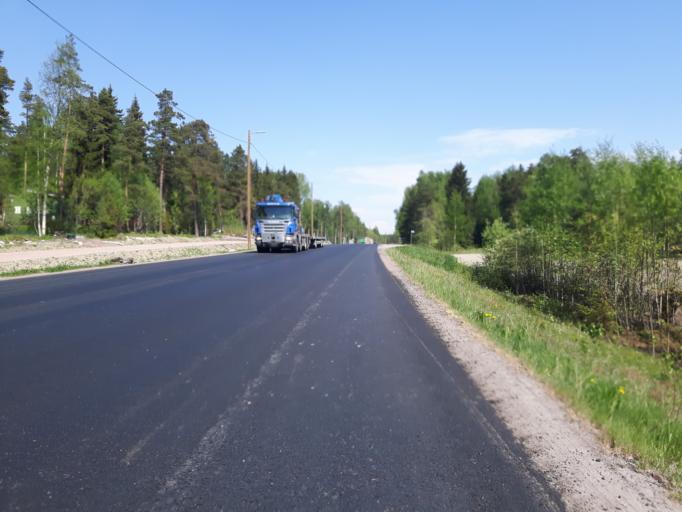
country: FI
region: Uusimaa
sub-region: Porvoo
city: Porvoo
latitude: 60.3603
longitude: 25.5376
